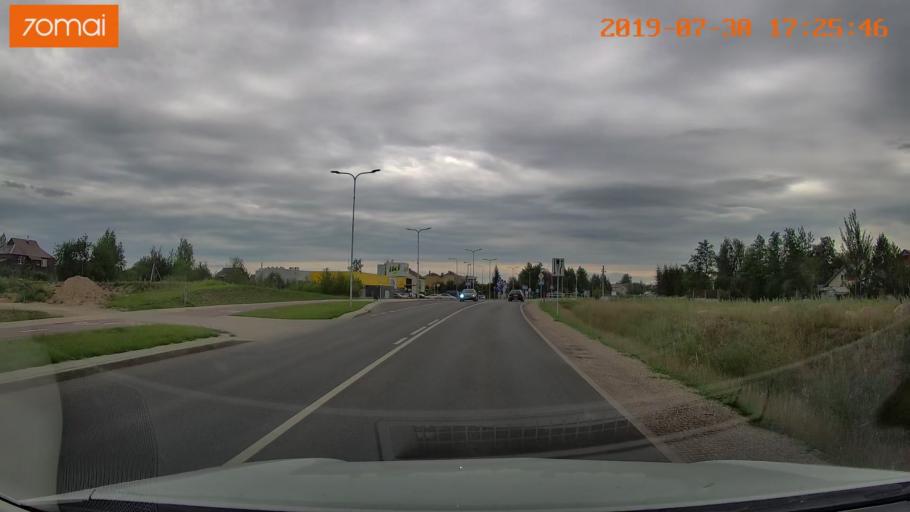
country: LT
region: Vilnius County
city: Rasos
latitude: 54.7263
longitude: 25.4122
